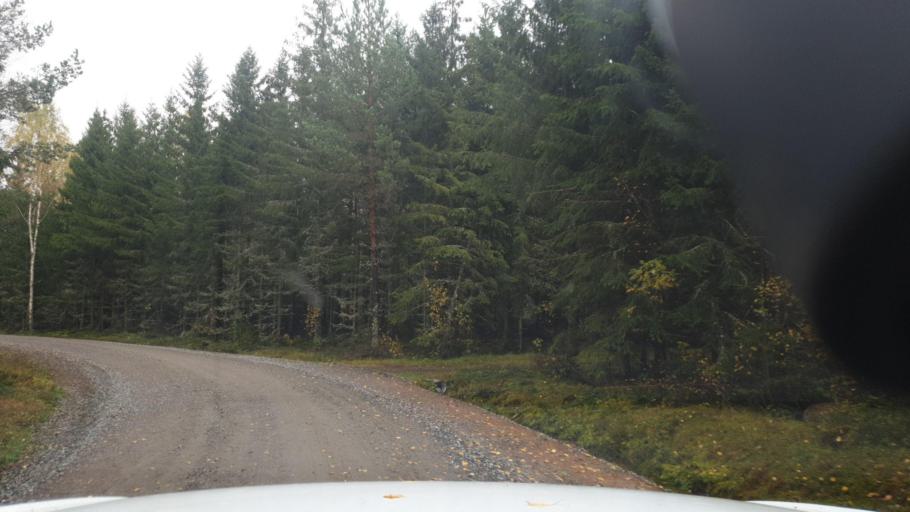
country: SE
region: Vaermland
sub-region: Karlstads Kommun
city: Edsvalla
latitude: 59.4813
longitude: 13.1421
